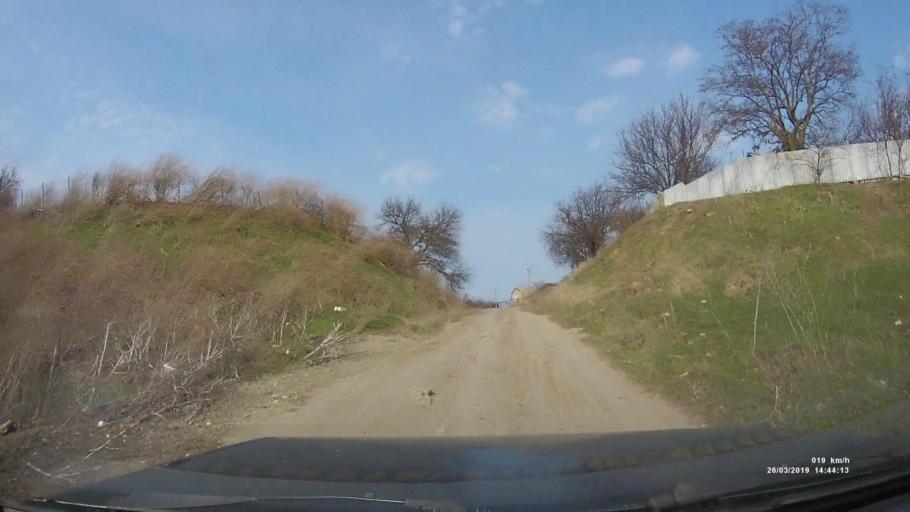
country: RU
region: Rostov
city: Novobessergenovka
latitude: 47.1769
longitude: 38.8622
